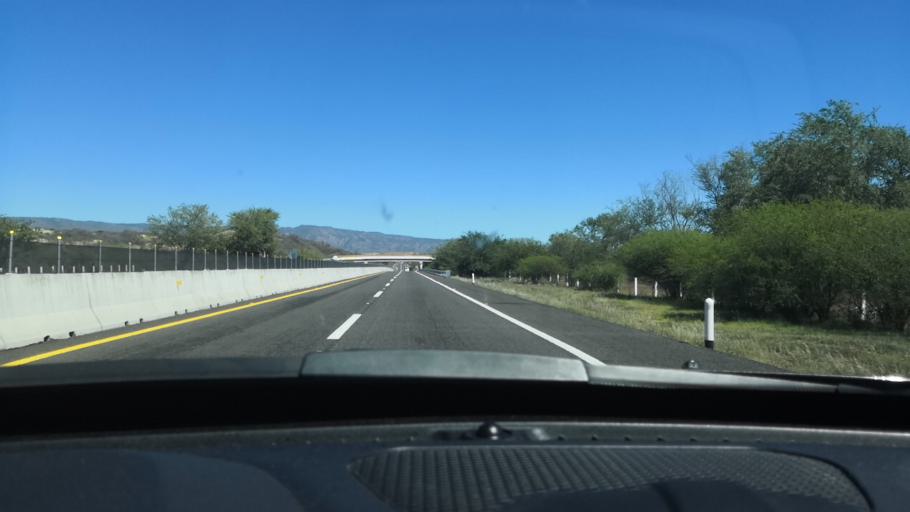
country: MX
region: Nayarit
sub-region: Ahuacatlan
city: Ahuacatlan
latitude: 21.0654
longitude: -104.4957
